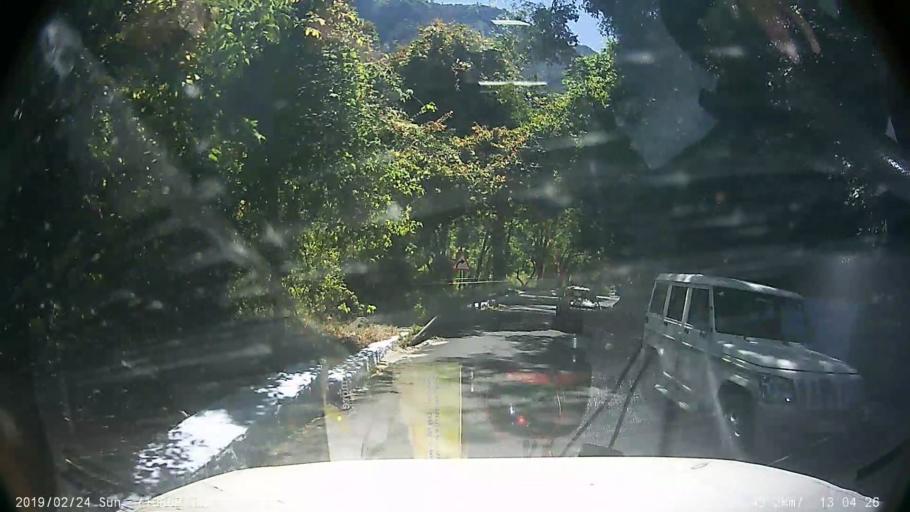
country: IN
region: Tamil Nadu
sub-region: Nilgiri
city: Wellington
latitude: 11.3360
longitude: 76.8276
